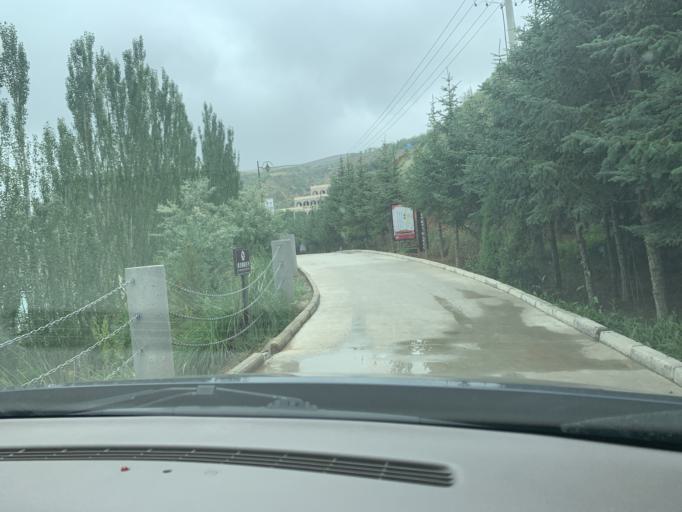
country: CN
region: Gansu Sheng
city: Gulang
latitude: 37.5616
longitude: 102.7425
